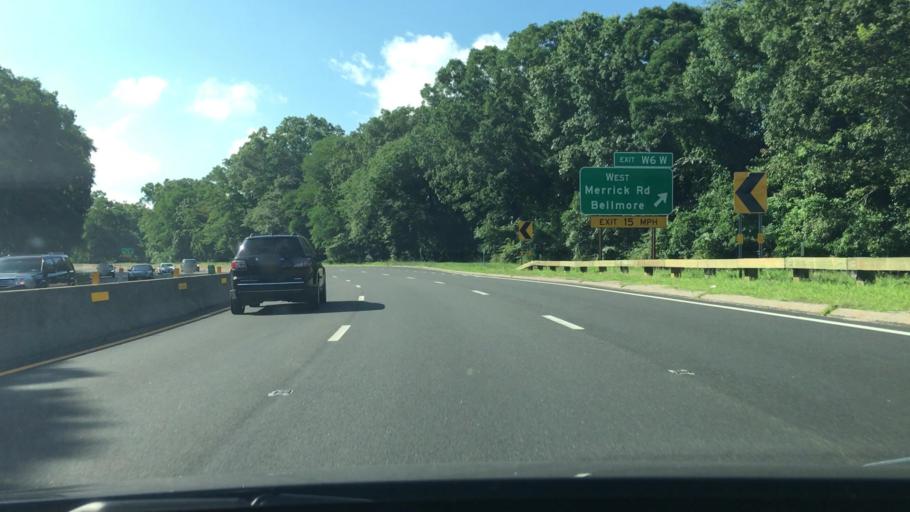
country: US
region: New York
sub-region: Nassau County
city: Bellmore
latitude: 40.6667
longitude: -73.5159
